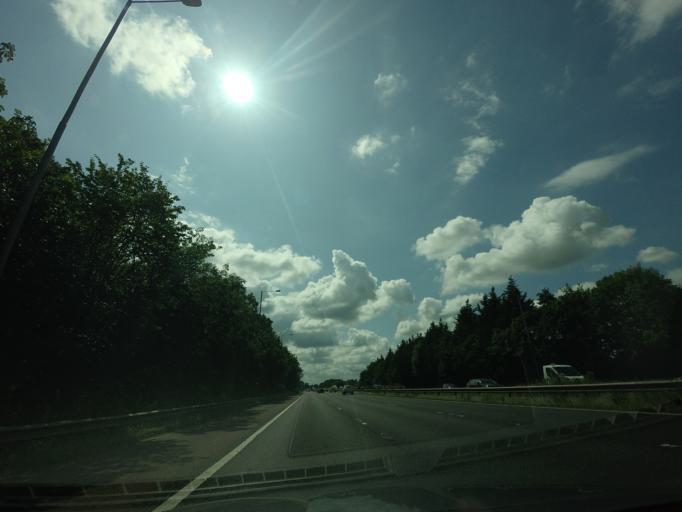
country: GB
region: England
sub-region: Lancashire
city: Clayton-le-Woods
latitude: 53.7002
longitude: -2.6773
